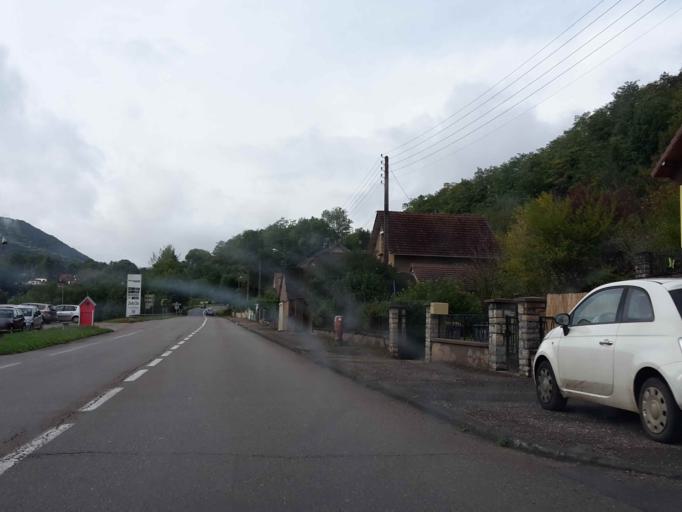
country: FR
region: Franche-Comte
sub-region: Departement du Doubs
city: Baume-les-Dames
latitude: 47.3516
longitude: 6.3491
